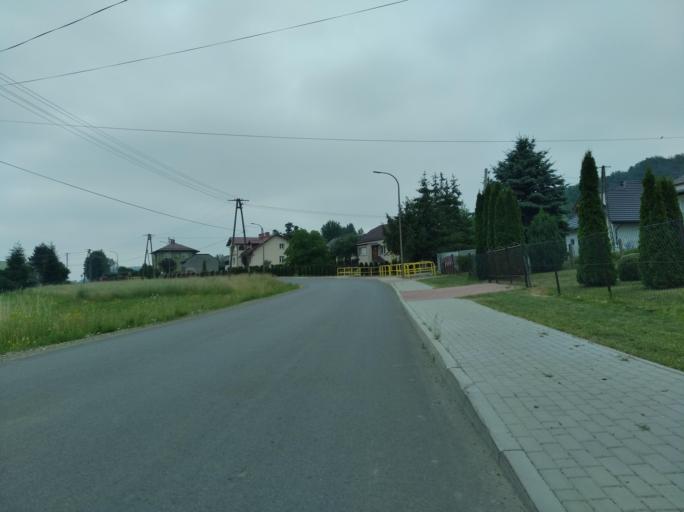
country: PL
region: Subcarpathian Voivodeship
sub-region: Powiat krosnienski
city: Rymanow
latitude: 49.6023
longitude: 21.9025
